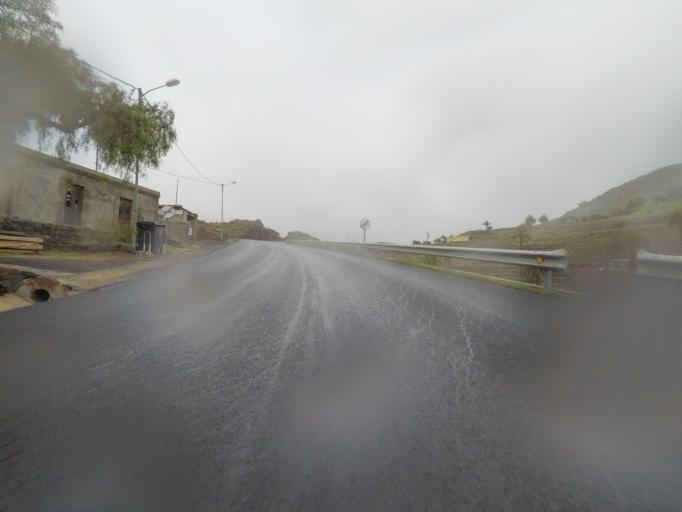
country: ES
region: Canary Islands
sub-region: Provincia de Santa Cruz de Tenerife
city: Alajero
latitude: 28.0756
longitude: -17.2080
